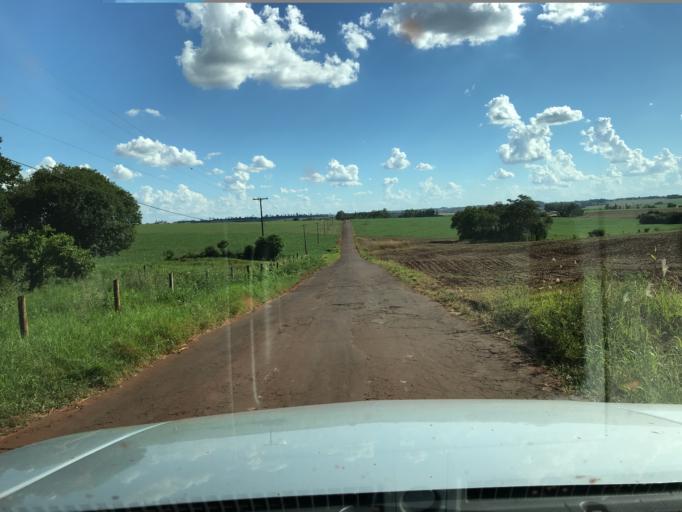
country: BR
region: Parana
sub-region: Palotina
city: Palotina
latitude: -24.2371
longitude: -53.7869
